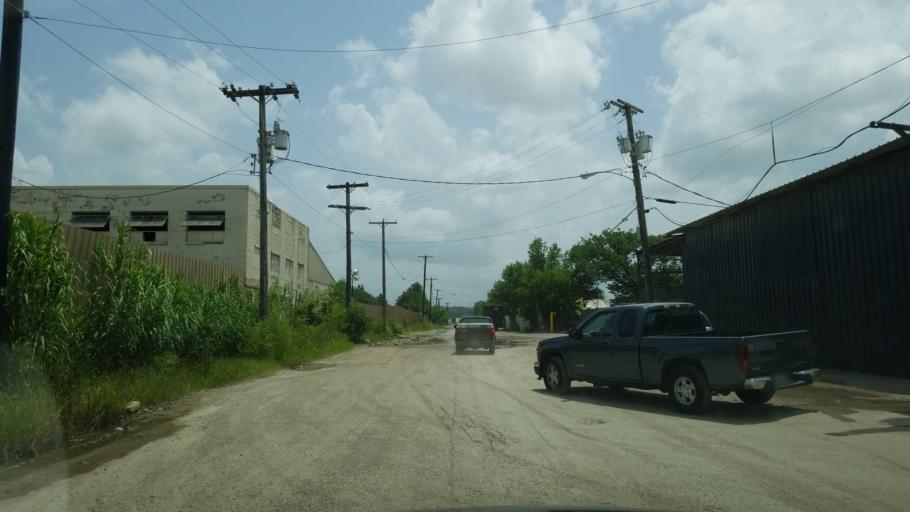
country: US
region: Texas
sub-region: Dallas County
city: Cockrell Hill
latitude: 32.7825
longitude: -96.8919
